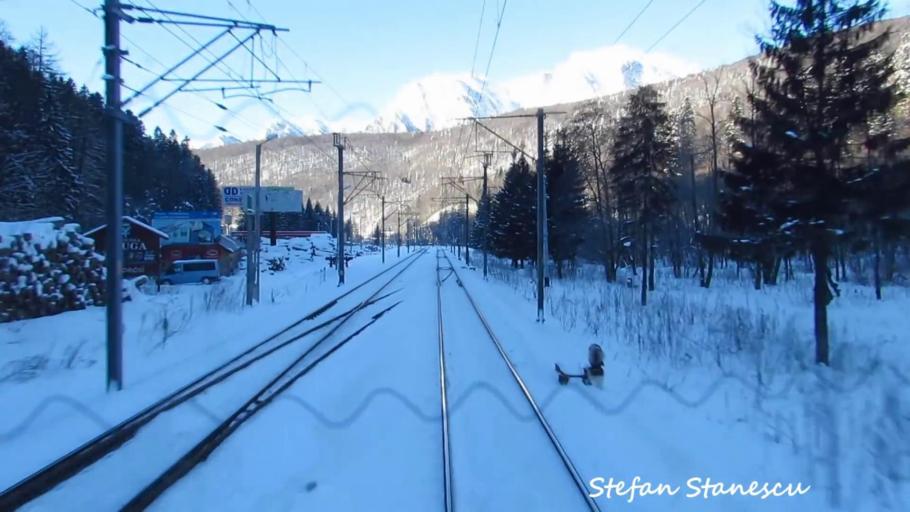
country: RO
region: Prahova
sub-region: Oras Azuga
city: Azuga
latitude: 45.4518
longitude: 25.5614
